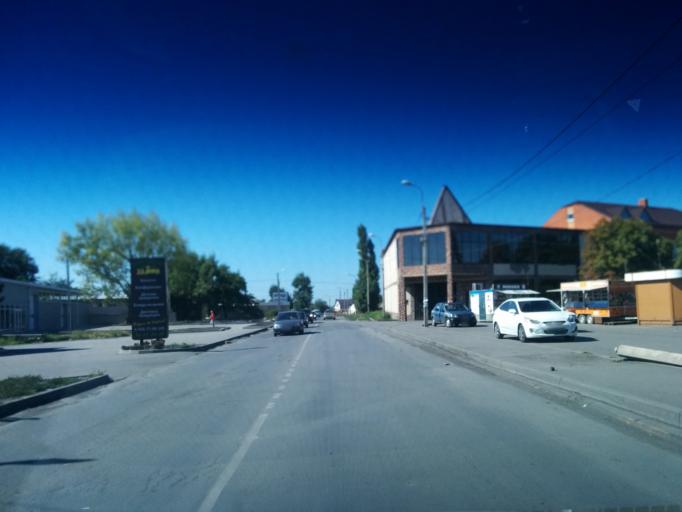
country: RU
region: Rostov
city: Shakhty
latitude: 47.6872
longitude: 40.2659
